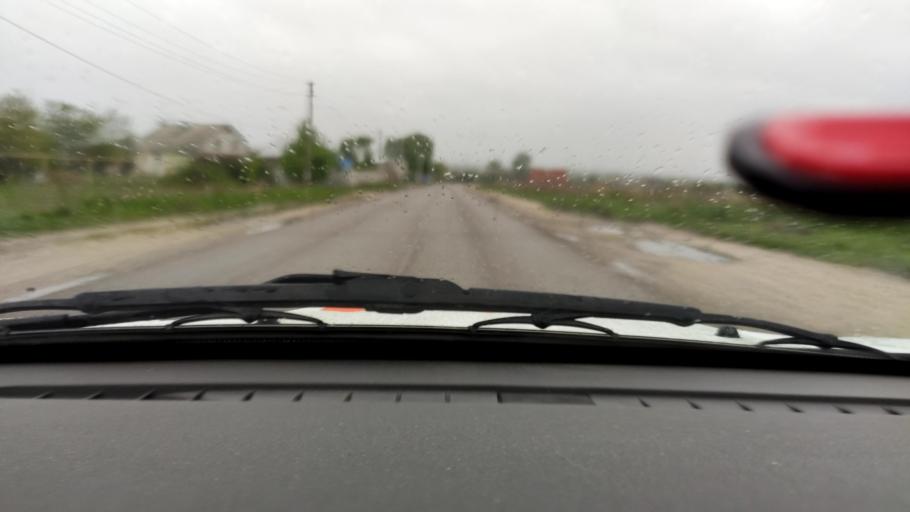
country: RU
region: Voronezj
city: Devitsa
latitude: 51.6324
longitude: 38.9287
